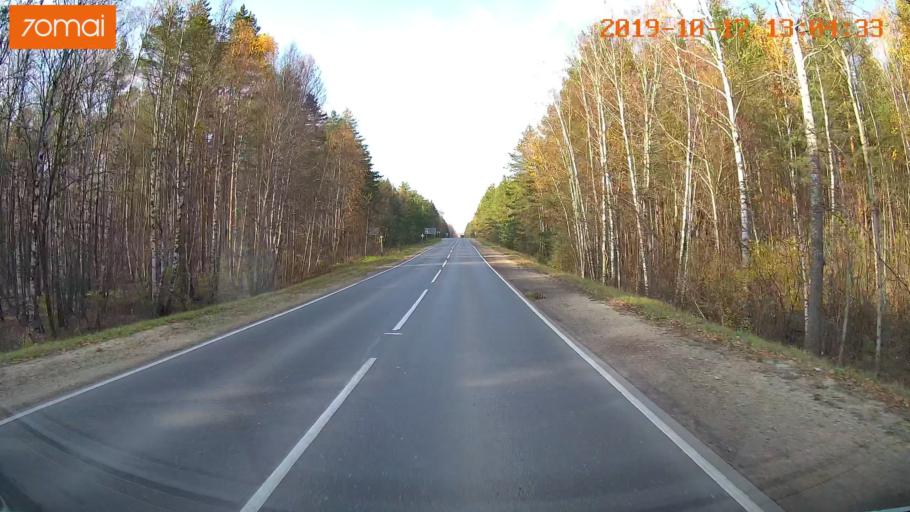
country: RU
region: Rjazan
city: Kasimov
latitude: 54.9628
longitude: 41.3422
